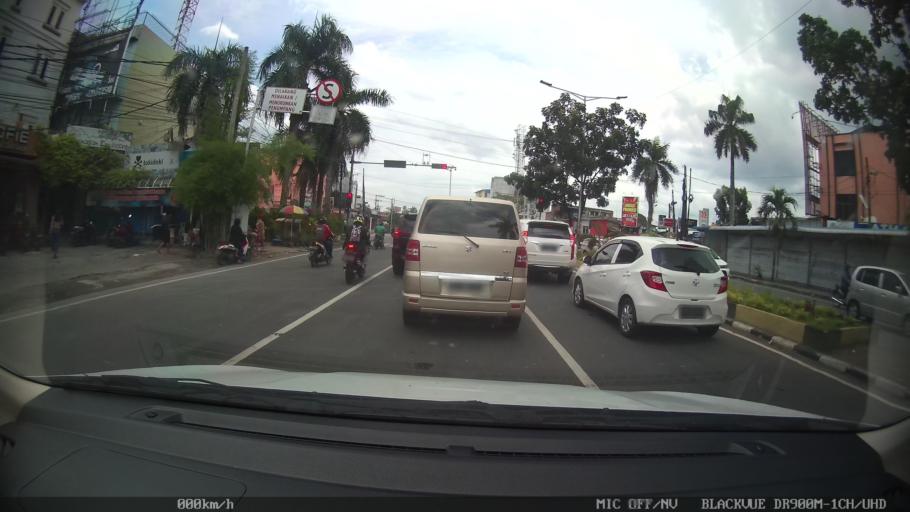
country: ID
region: North Sumatra
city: Medan
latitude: 3.6053
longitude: 98.6458
